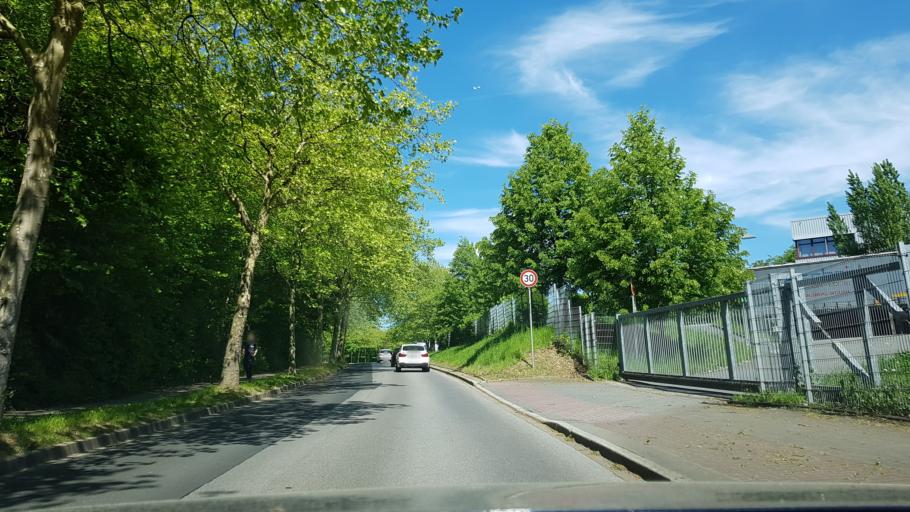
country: DE
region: North Rhine-Westphalia
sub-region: Regierungsbezirk Dusseldorf
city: Heiligenhaus
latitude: 51.3222
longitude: 6.9525
